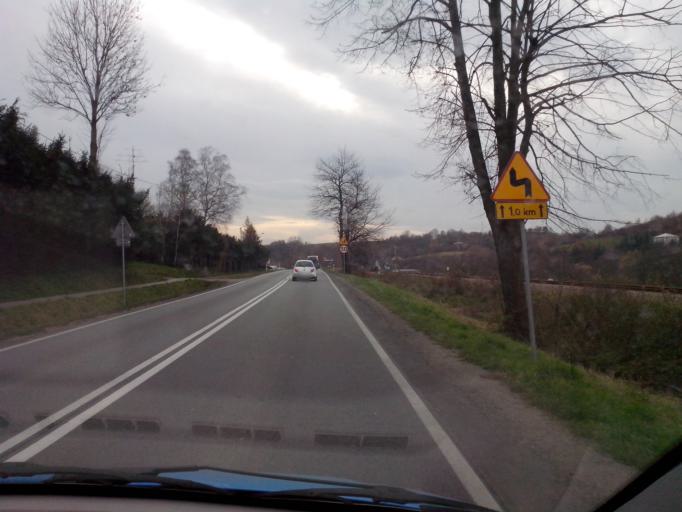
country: PL
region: Subcarpathian Voivodeship
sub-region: Powiat strzyzowski
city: Strzyzow
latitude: 49.8777
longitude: 21.8194
